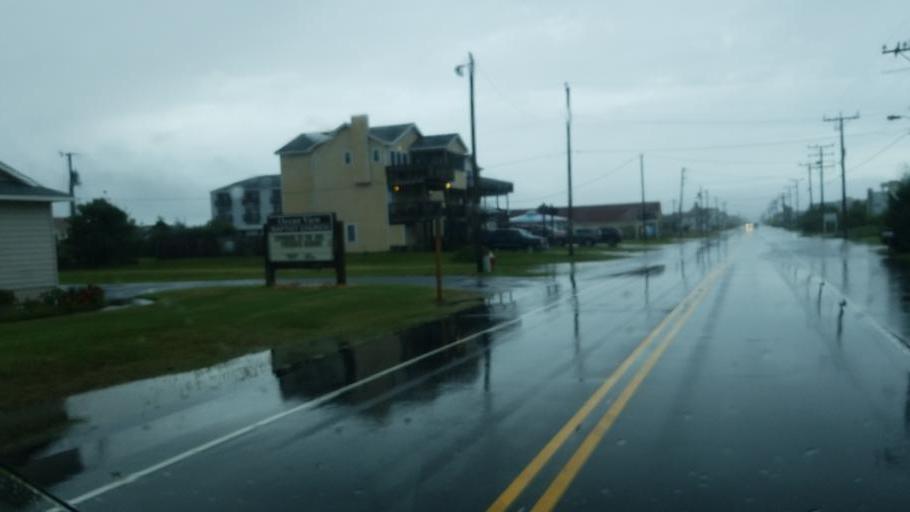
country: US
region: North Carolina
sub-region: Dare County
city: Kill Devil Hills
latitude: 36.0089
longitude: -75.6543
